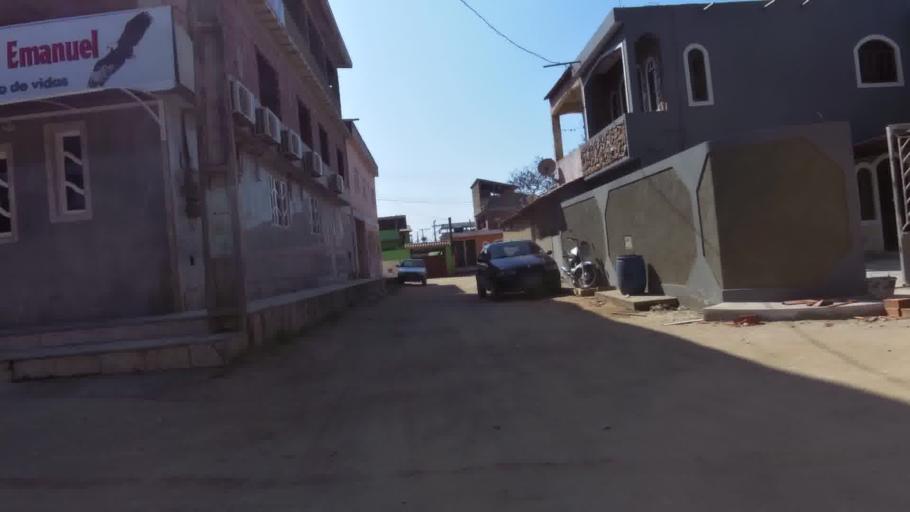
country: BR
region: Espirito Santo
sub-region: Itapemirim
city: Itapemirim
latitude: -21.0211
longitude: -40.8166
